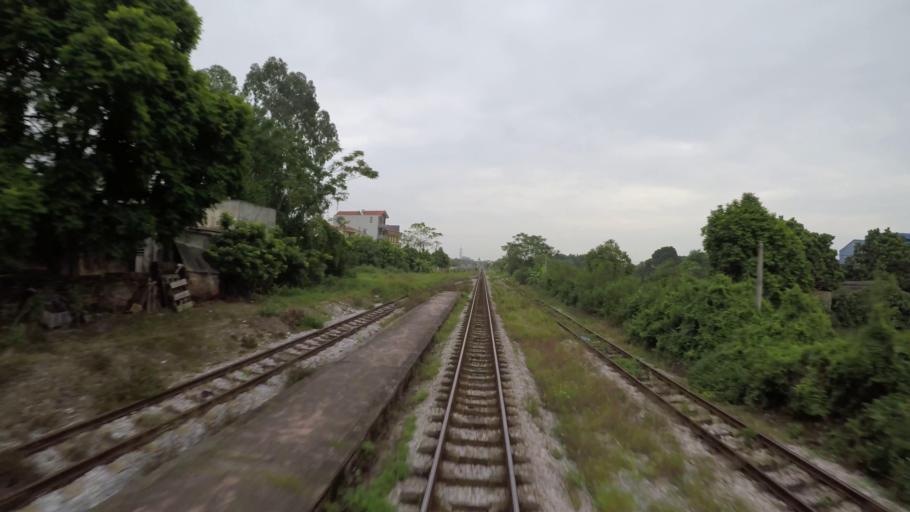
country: VN
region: Hung Yen
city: Ban Yen Nhan
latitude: 20.9854
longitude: 106.0479
